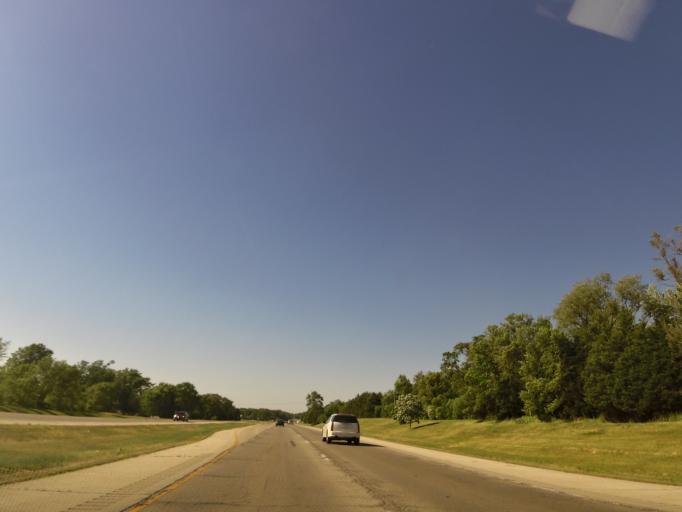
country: US
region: Illinois
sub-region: Winnebago County
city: Roscoe
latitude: 42.4061
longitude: -89.0115
